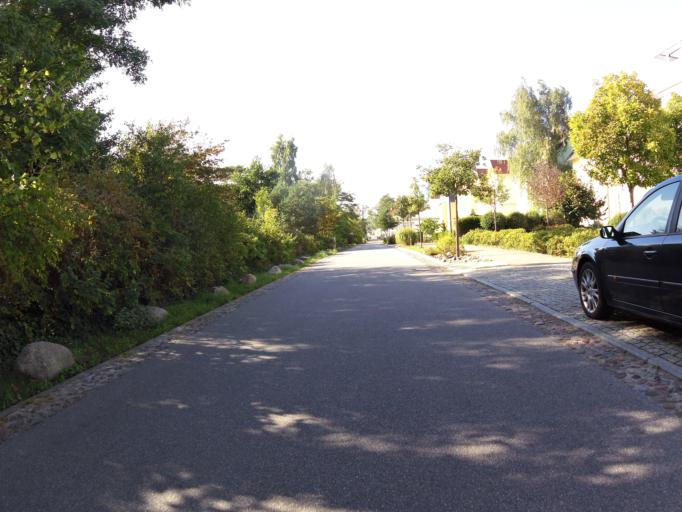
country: DE
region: Mecklenburg-Vorpommern
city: Seebad Heringsdorf
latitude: 53.9366
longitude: 14.2003
